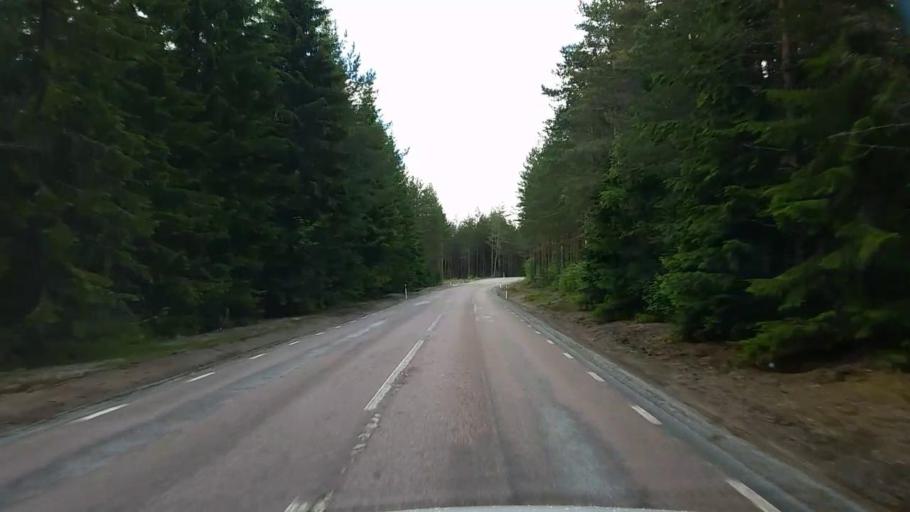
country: SE
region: Vaestmanland
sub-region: Fagersta Kommun
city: Fagersta
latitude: 59.8997
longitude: 15.8200
